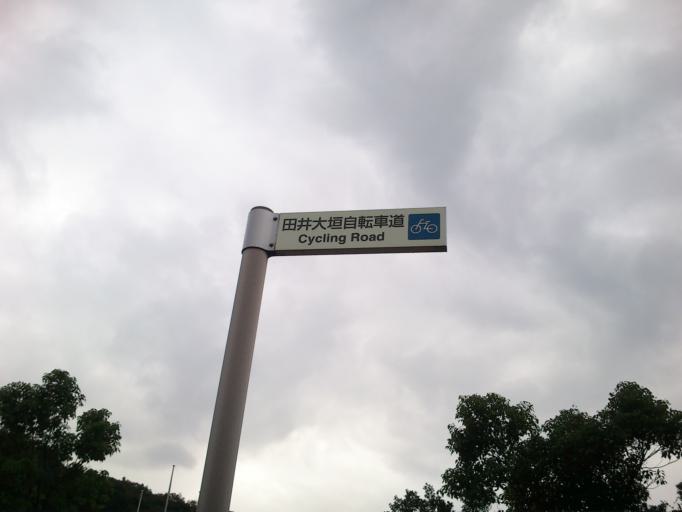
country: JP
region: Kyoto
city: Miyazu
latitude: 35.5823
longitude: 135.2326
